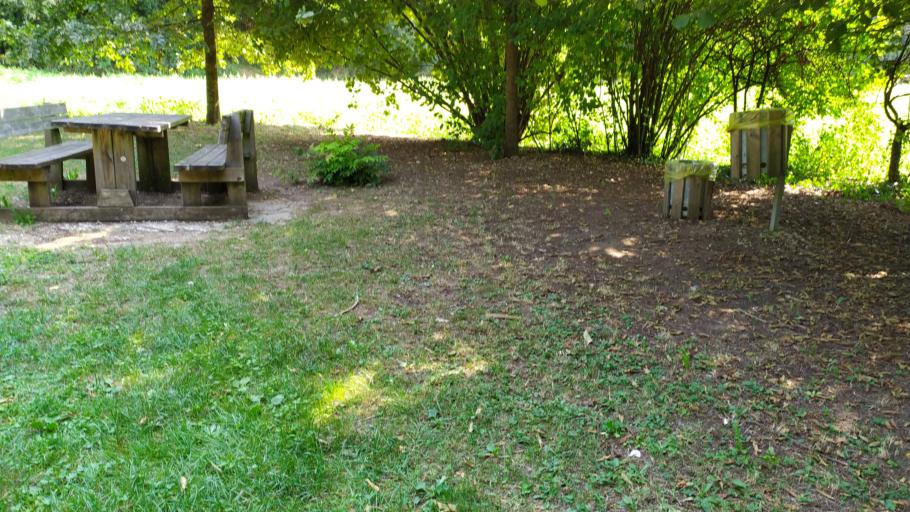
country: IT
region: Veneto
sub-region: Provincia di Vicenza
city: Arcugnano-Torri
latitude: 45.4652
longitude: 11.5453
